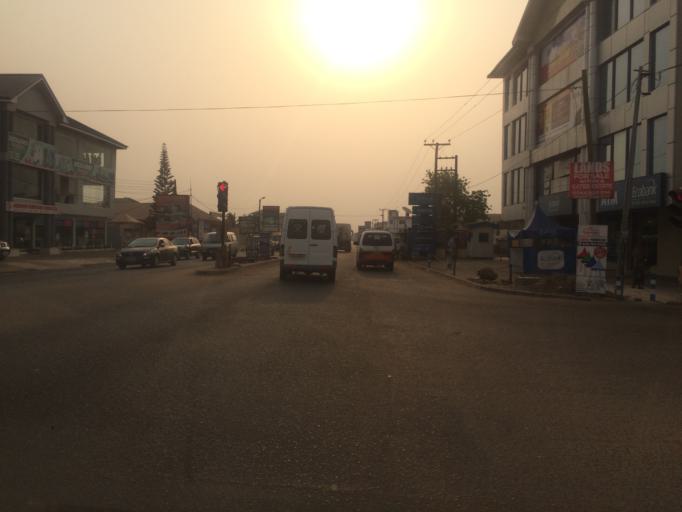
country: GH
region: Greater Accra
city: Nungua
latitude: 5.6289
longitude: -0.0903
